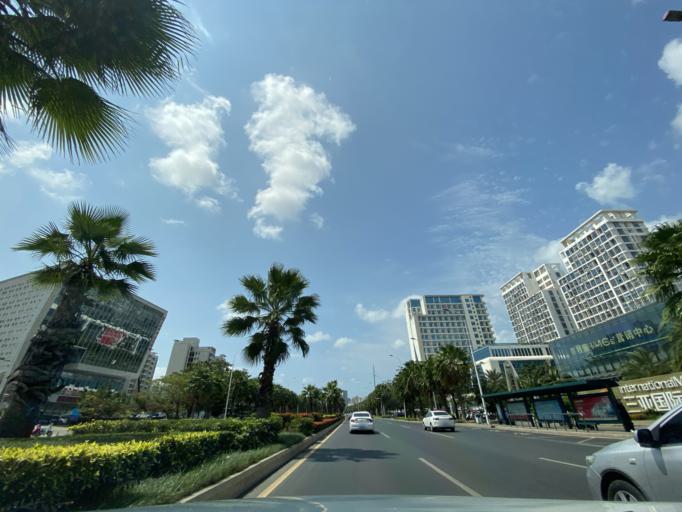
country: CN
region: Hainan
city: Sanya
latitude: 18.2893
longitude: 109.5234
